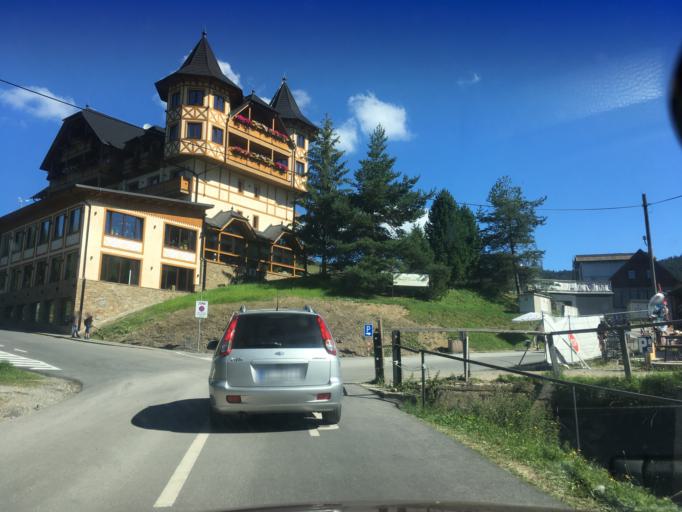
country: SK
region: Presovsky
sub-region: Okres Poprad
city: Zdiar
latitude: 49.2714
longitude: 20.3094
